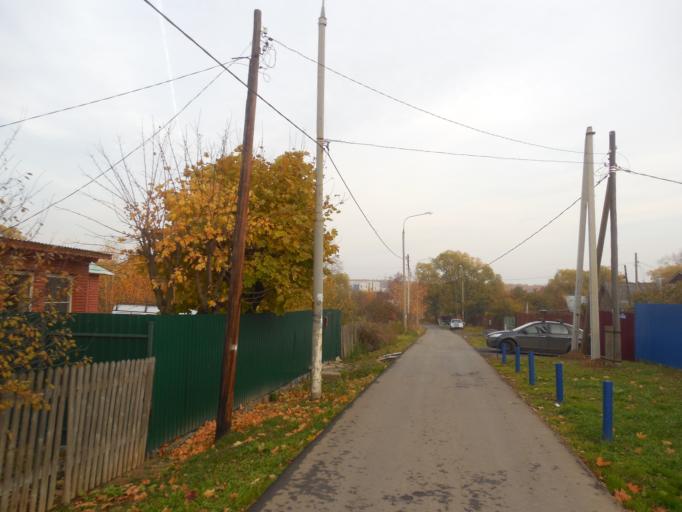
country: RU
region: Moskovskaya
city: Shcherbinka
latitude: 55.4990
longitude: 37.5906
